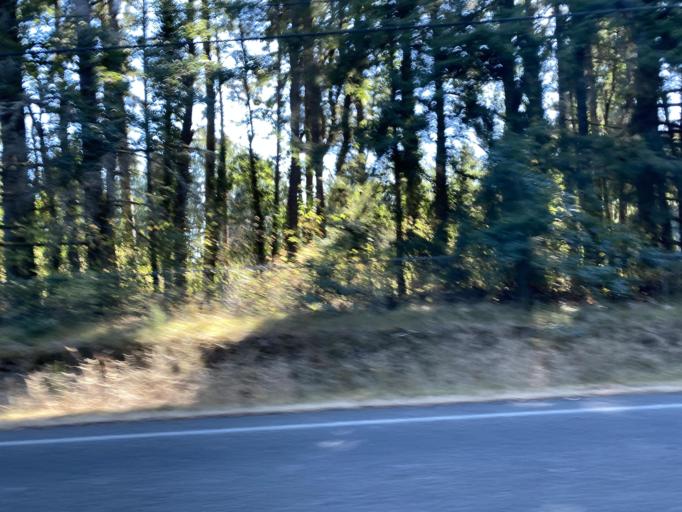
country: US
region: Washington
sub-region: Thurston County
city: Tanglewilde-Thompson Place
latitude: 47.0061
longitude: -122.7386
